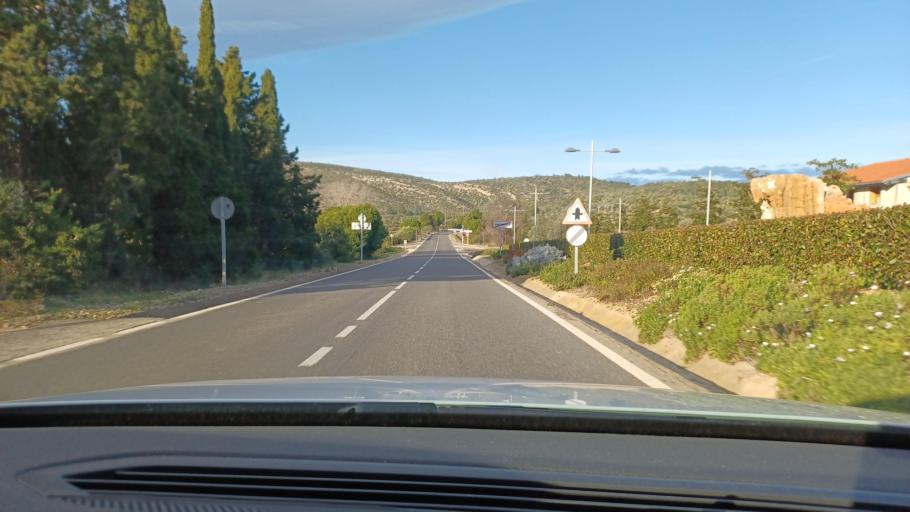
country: ES
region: Catalonia
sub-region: Provincia de Tarragona
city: Masdenverge
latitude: 40.6699
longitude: 0.5186
